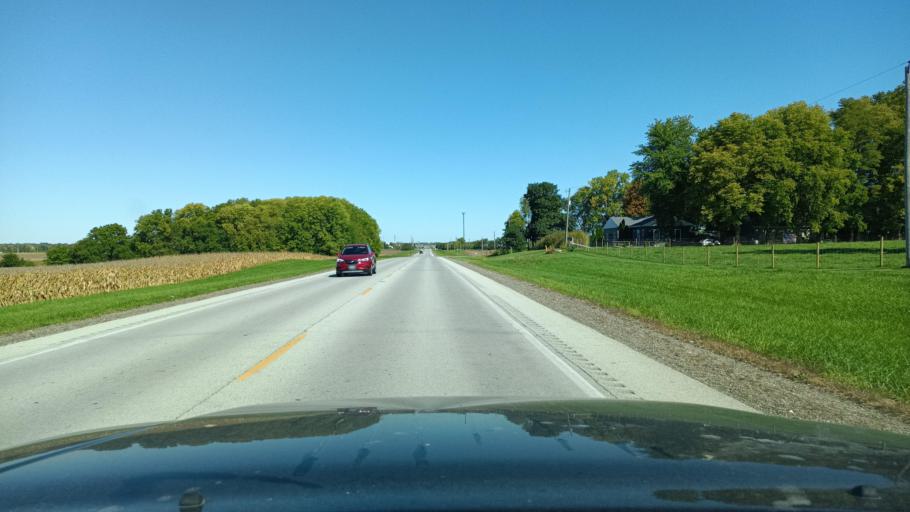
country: US
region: Illinois
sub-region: Champaign County
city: Urbana
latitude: 40.0748
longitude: -88.1620
